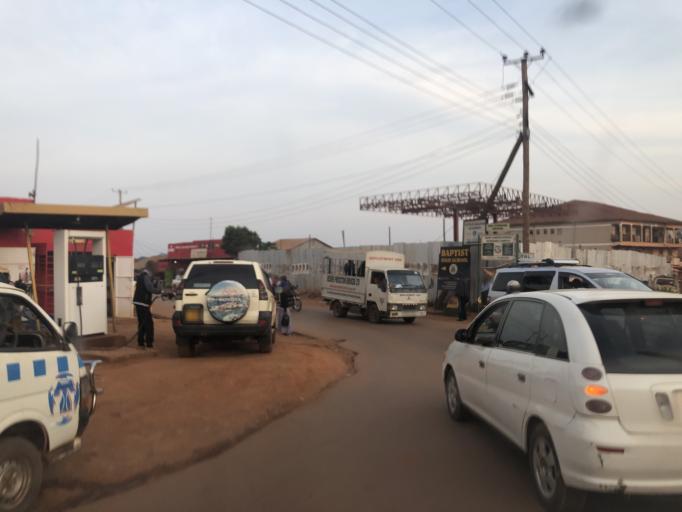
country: UG
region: Central Region
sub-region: Kampala District
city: Kampala
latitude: 0.2736
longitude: 32.5466
